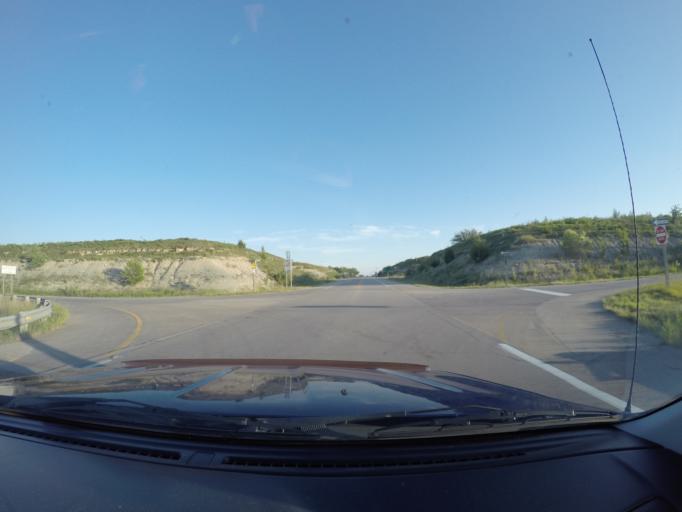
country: US
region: Kansas
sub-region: Wabaunsee County
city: Alma
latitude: 39.0653
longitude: -96.2891
